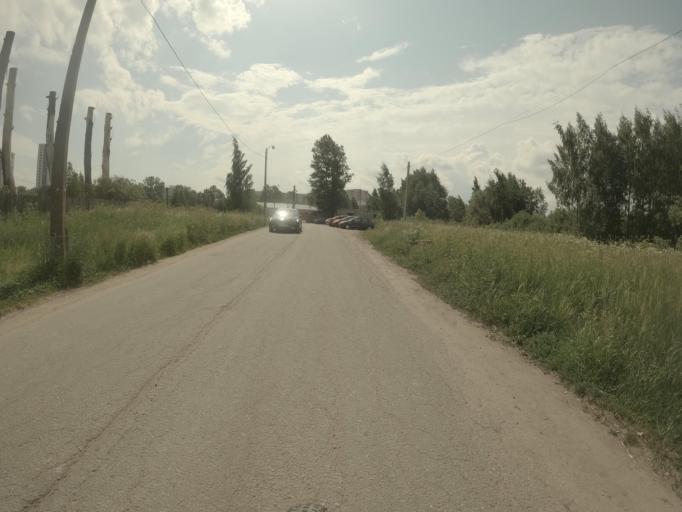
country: RU
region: St.-Petersburg
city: Krasnogvargeisky
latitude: 59.9621
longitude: 30.4743
